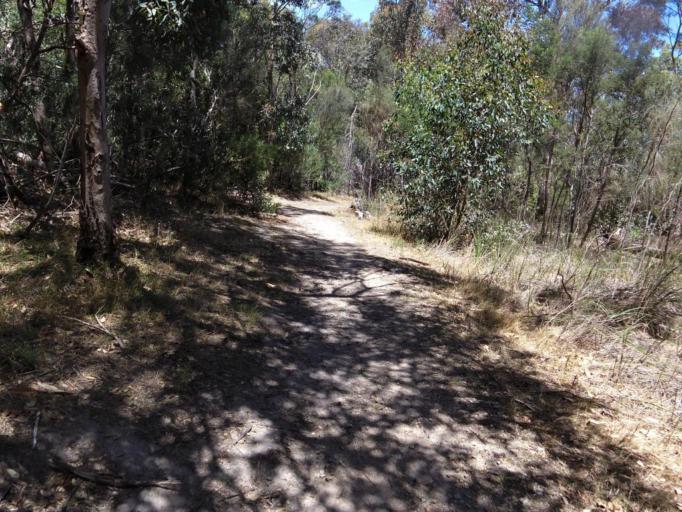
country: AU
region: Victoria
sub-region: Mornington Peninsula
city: Safety Beach
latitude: -38.2951
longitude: 145.0012
